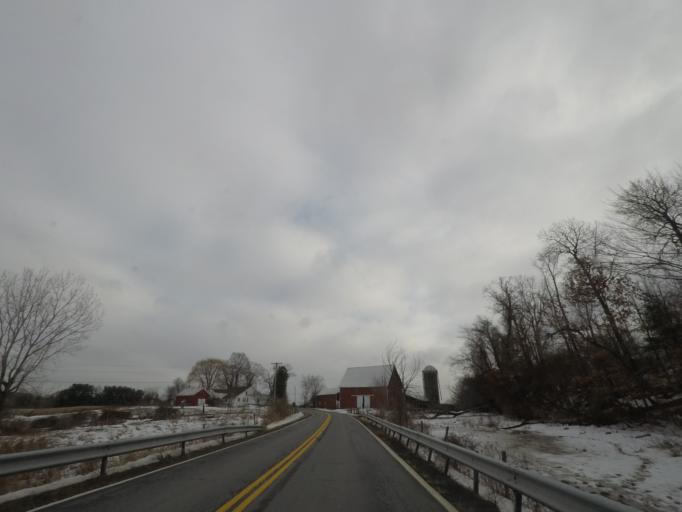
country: US
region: New York
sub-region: Schenectady County
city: Rotterdam
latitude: 42.7314
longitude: -73.9601
